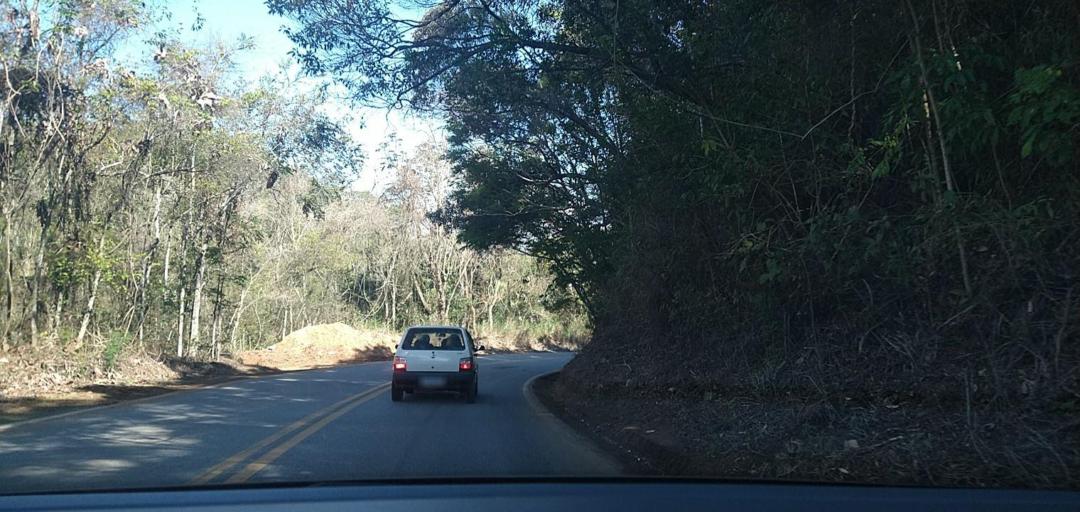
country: BR
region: Minas Gerais
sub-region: Alvinopolis
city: Alvinopolis
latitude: -20.0368
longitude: -43.0331
